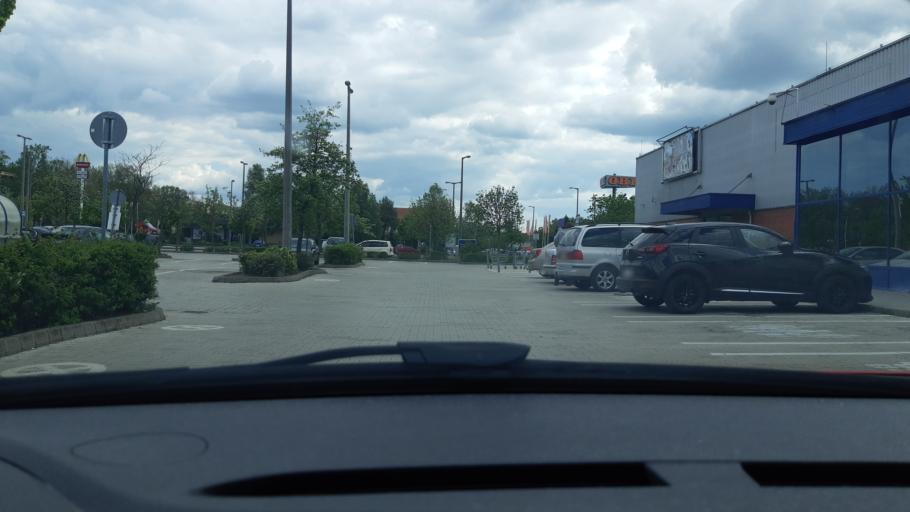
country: HU
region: Somogy
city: Kaposvar
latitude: 46.3605
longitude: 17.7824
